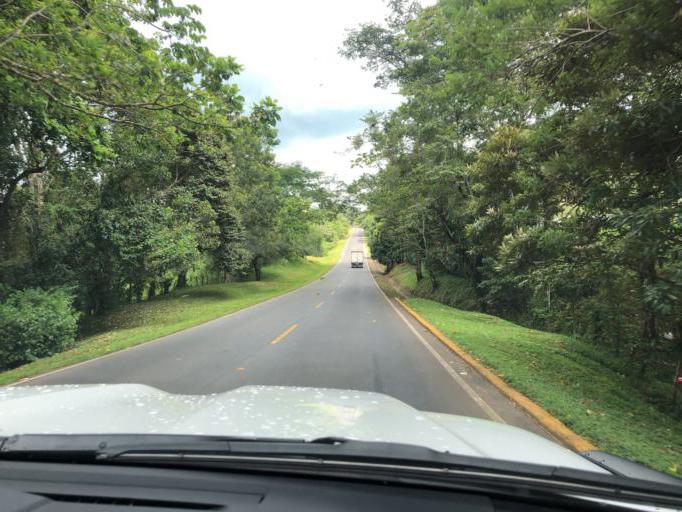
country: NI
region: Chontales
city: Villa Sandino
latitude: 11.9978
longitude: -84.8420
